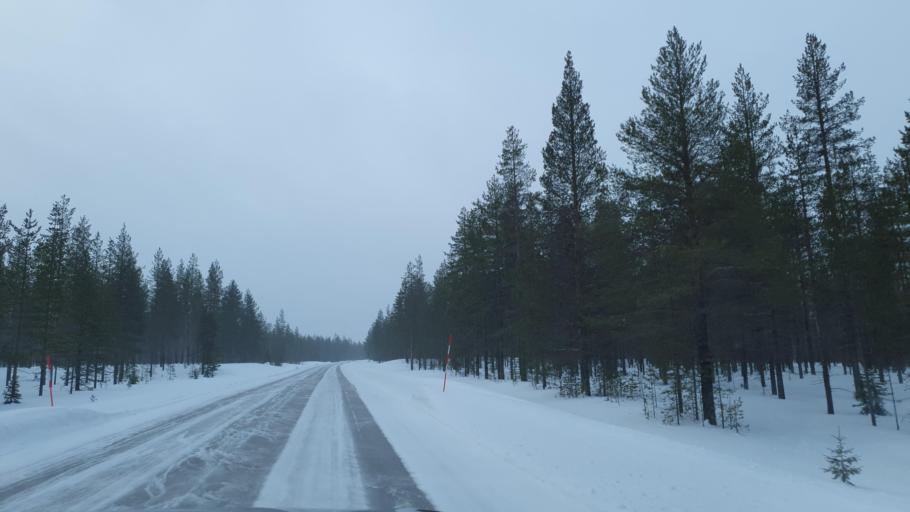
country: FI
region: Lapland
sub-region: Tunturi-Lappi
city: Kolari
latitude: 67.5083
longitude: 23.9038
